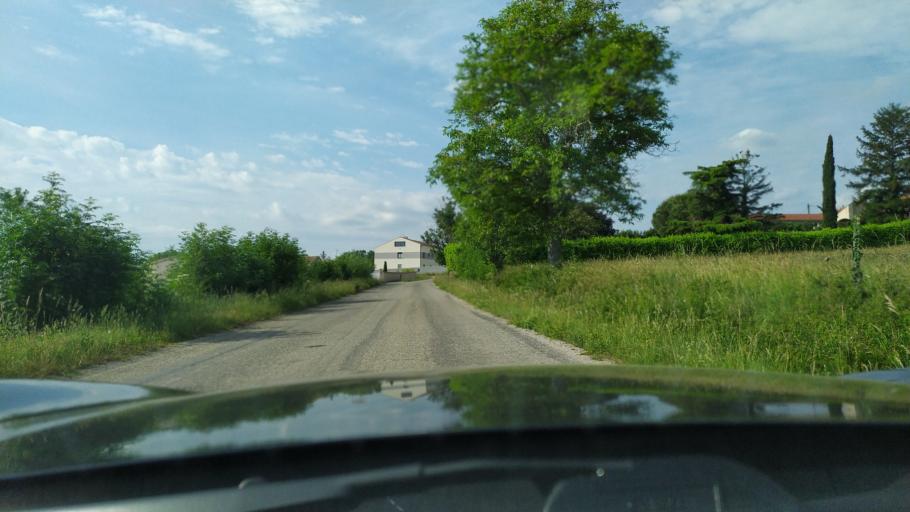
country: FR
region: Rhone-Alpes
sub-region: Departement de l'Ardeche
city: Felines
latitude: 45.3030
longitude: 4.7293
